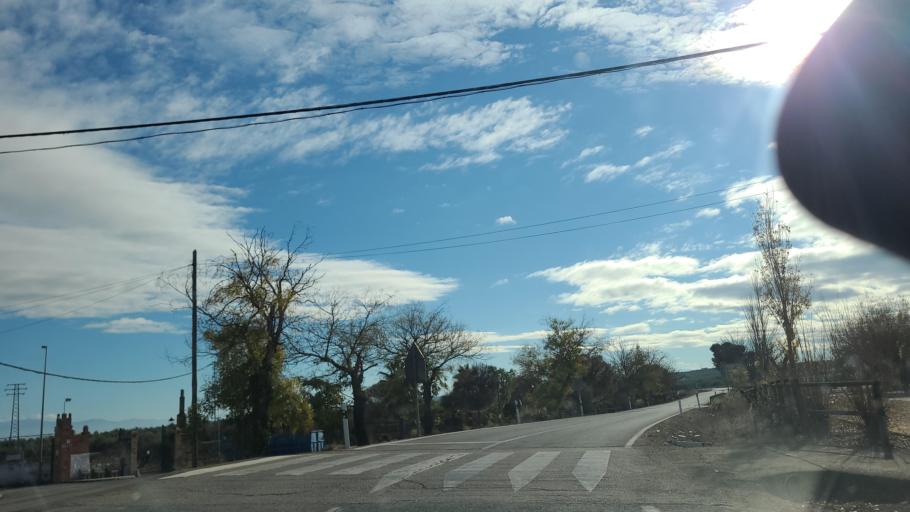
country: ES
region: Andalusia
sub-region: Provincia de Jaen
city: Espeluy
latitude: 38.0309
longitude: -3.8629
